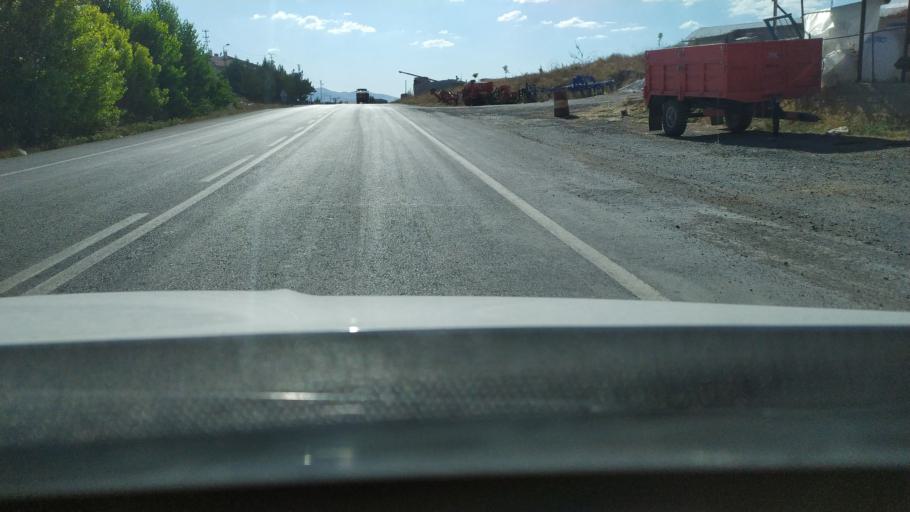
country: TR
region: Kayseri
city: Felahiye
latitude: 39.0948
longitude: 35.5761
